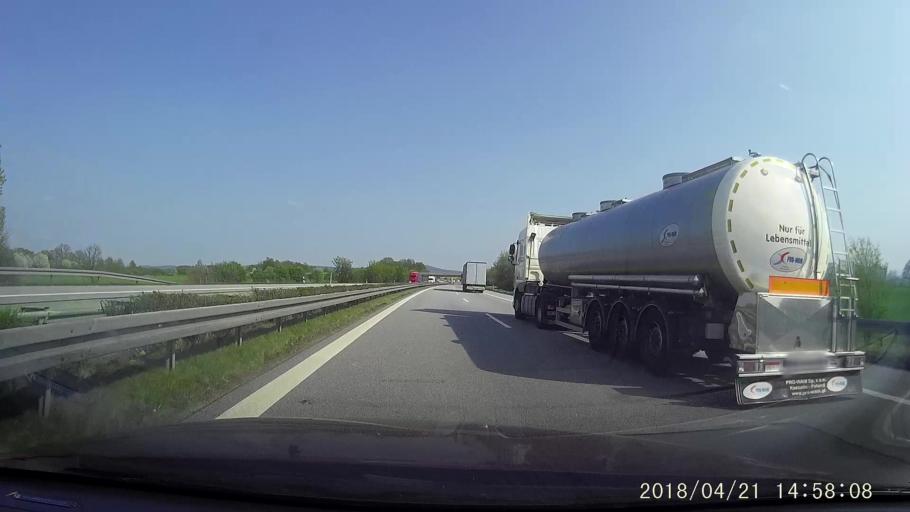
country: DE
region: Saxony
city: Weissenberg
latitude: 51.2119
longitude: 14.7264
